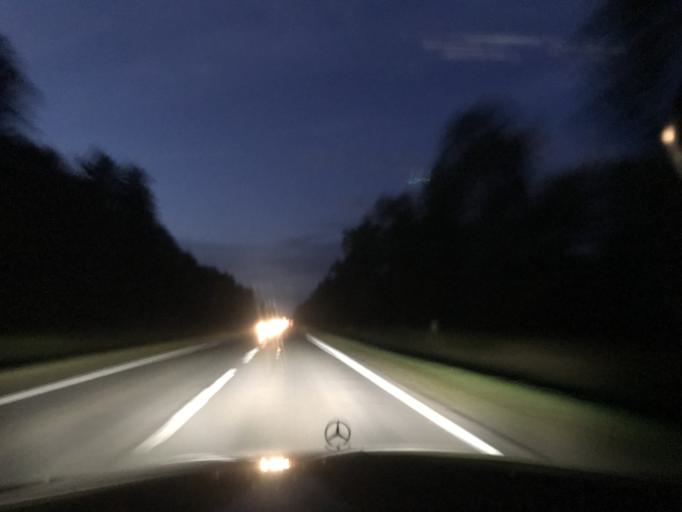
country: BY
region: Brest
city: Brest
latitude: 52.0290
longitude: 23.7296
